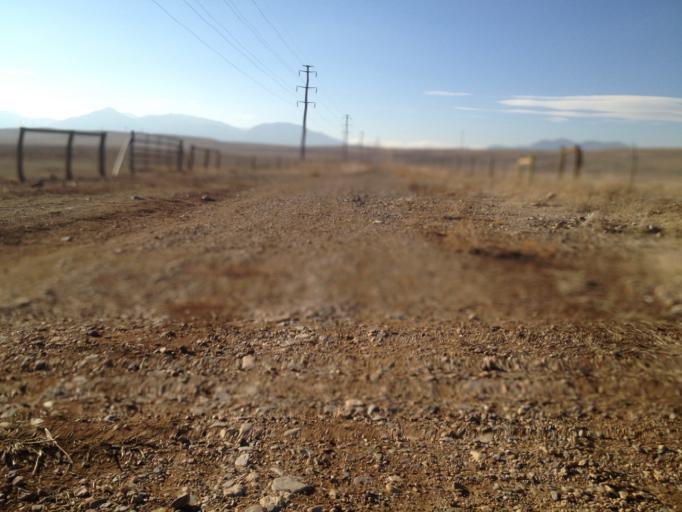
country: US
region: Colorado
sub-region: Boulder County
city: Superior
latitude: 39.9287
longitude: -105.1714
